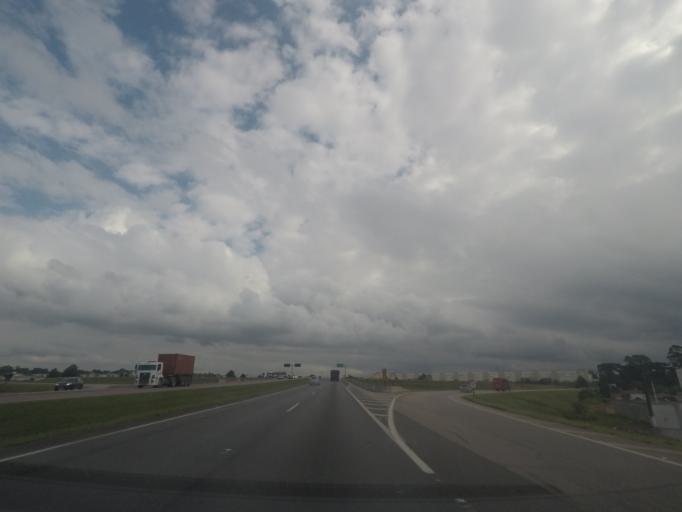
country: BR
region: Parana
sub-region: Sao Jose Dos Pinhais
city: Sao Jose dos Pinhais
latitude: -25.5086
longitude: -49.1260
